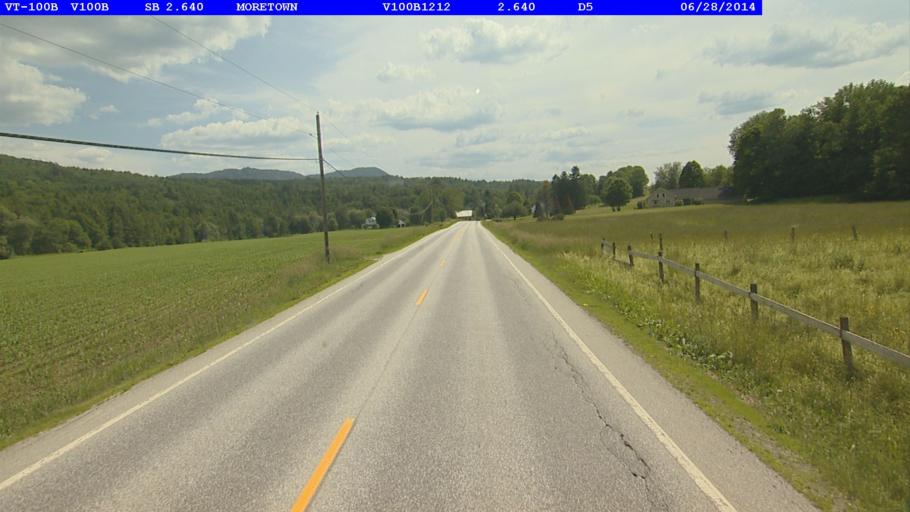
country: US
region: Vermont
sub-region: Washington County
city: Waterbury
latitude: 44.2673
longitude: -72.7466
